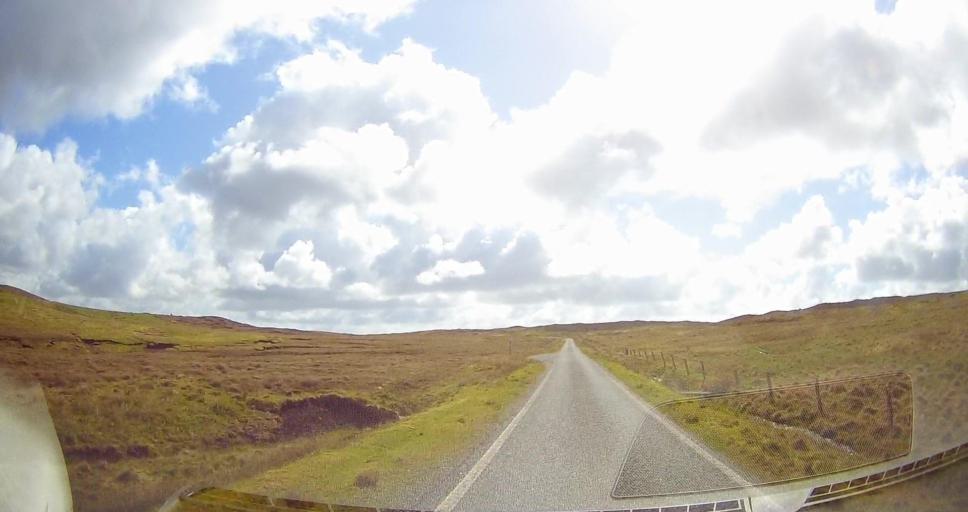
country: GB
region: Scotland
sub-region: Shetland Islands
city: Lerwick
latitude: 60.5034
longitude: -1.3931
